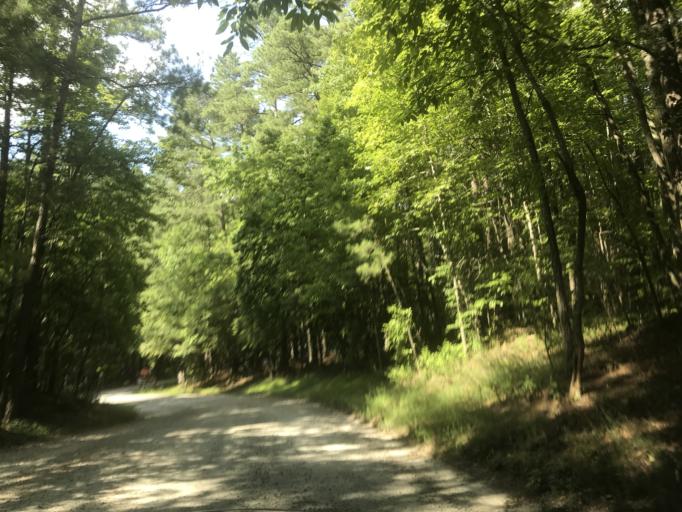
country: US
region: North Carolina
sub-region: Wake County
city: Morrisville
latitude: 35.8775
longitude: -78.7576
